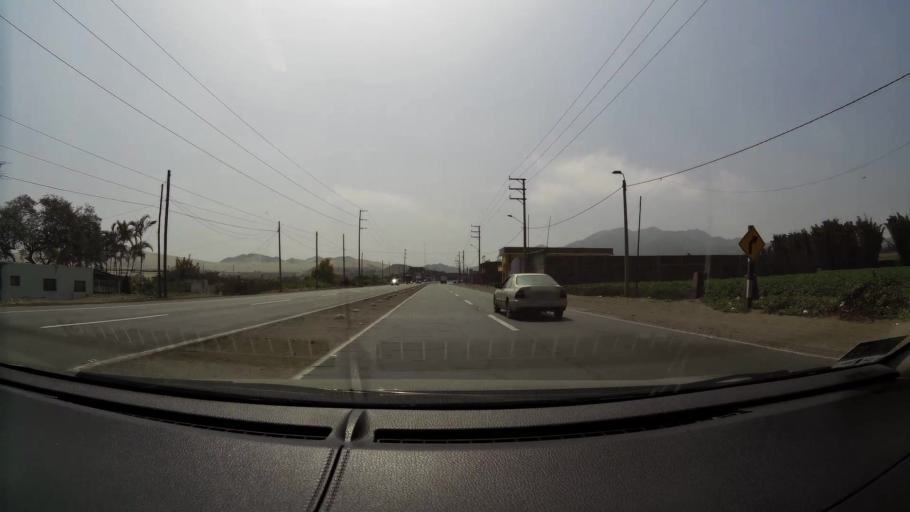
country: PE
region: Lima
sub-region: Provincia de Huaral
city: Chancay
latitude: -11.4958
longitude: -77.3030
